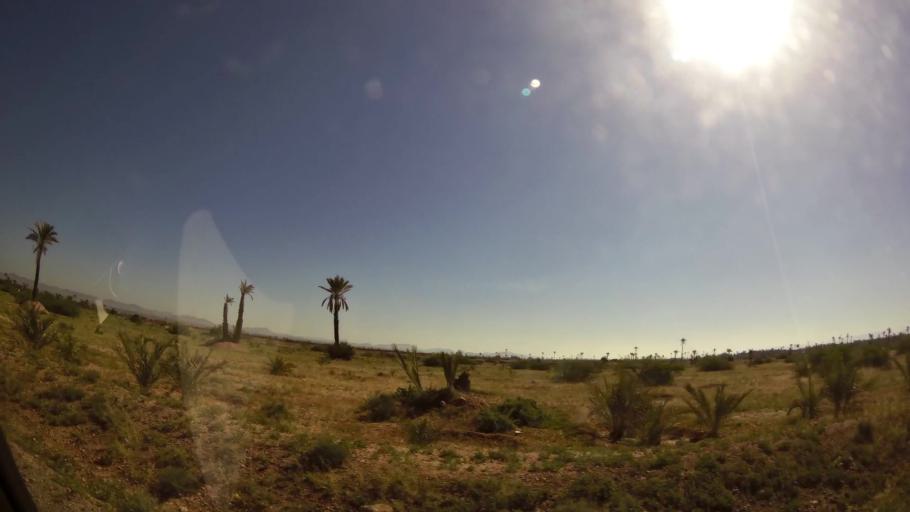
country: MA
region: Marrakech-Tensift-Al Haouz
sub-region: Marrakech
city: Marrakesh
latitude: 31.6674
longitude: -7.9530
